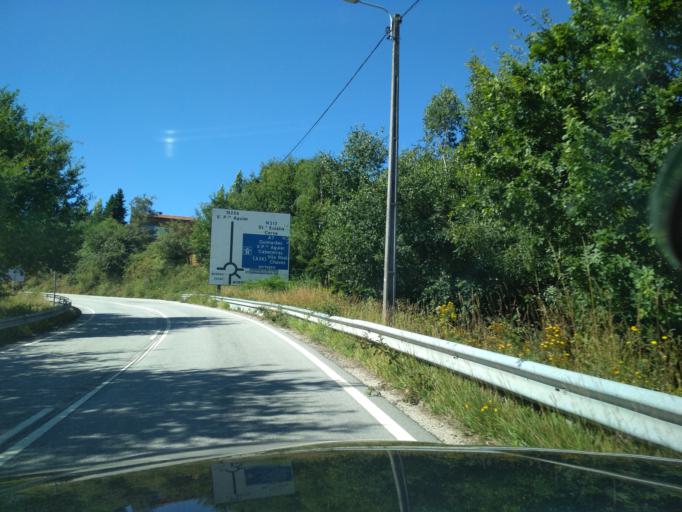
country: PT
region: Vila Real
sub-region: Ribeira de Pena
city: Ribeira de Pena
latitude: 41.5034
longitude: -7.7954
